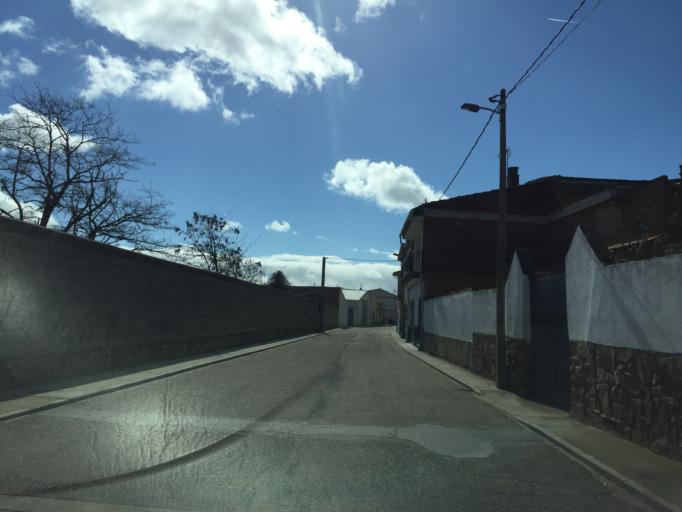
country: ES
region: Castille and Leon
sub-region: Provincia de Zamora
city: Montamarta
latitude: 41.6481
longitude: -5.8044
